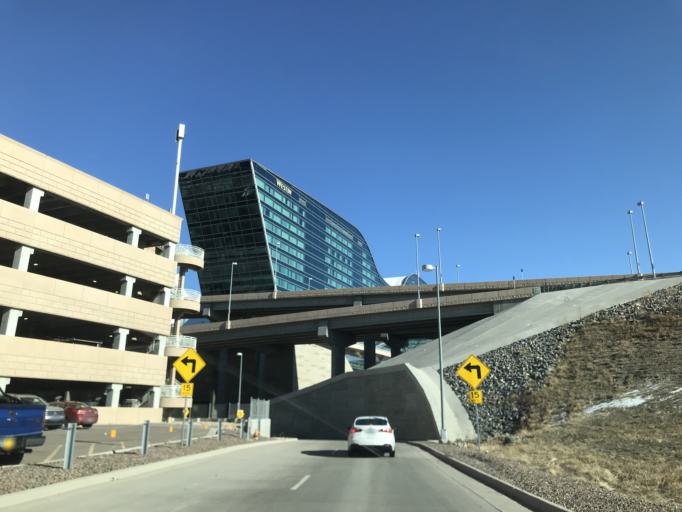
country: US
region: Colorado
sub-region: Weld County
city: Lochbuie
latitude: 39.8470
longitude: -104.6760
